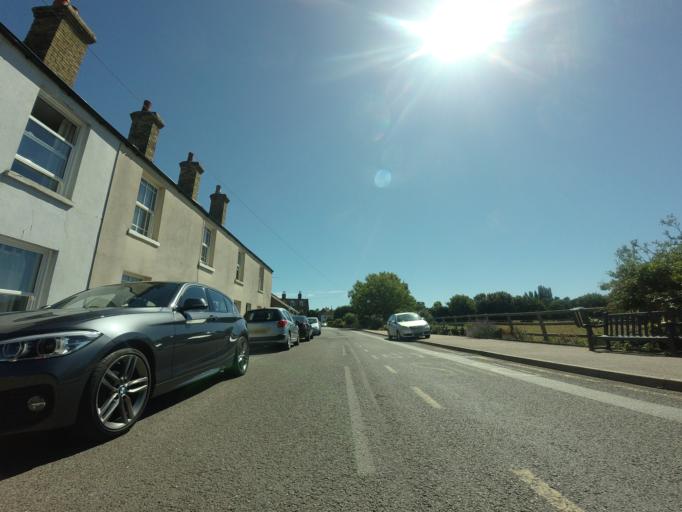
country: GB
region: England
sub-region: Kent
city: Ash
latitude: 51.2784
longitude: 1.2822
